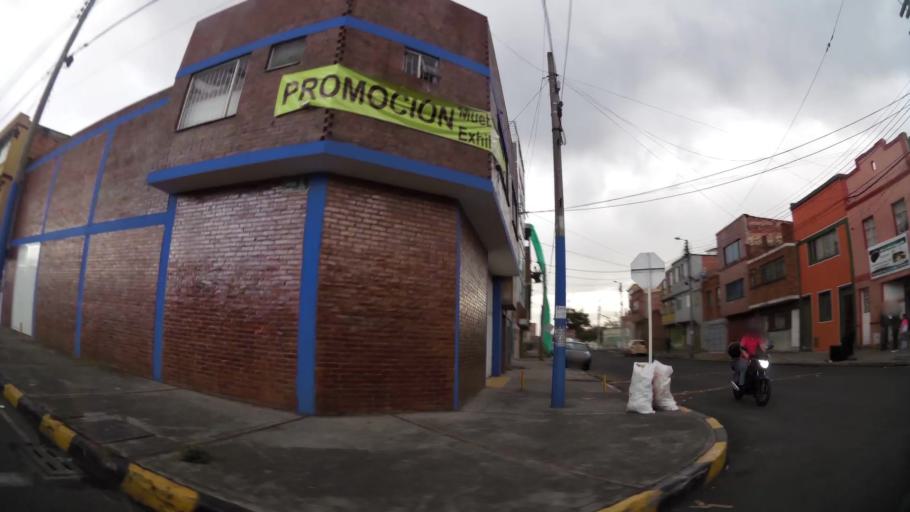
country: CO
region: Bogota D.C.
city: Barrio San Luis
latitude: 4.6684
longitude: -74.0756
